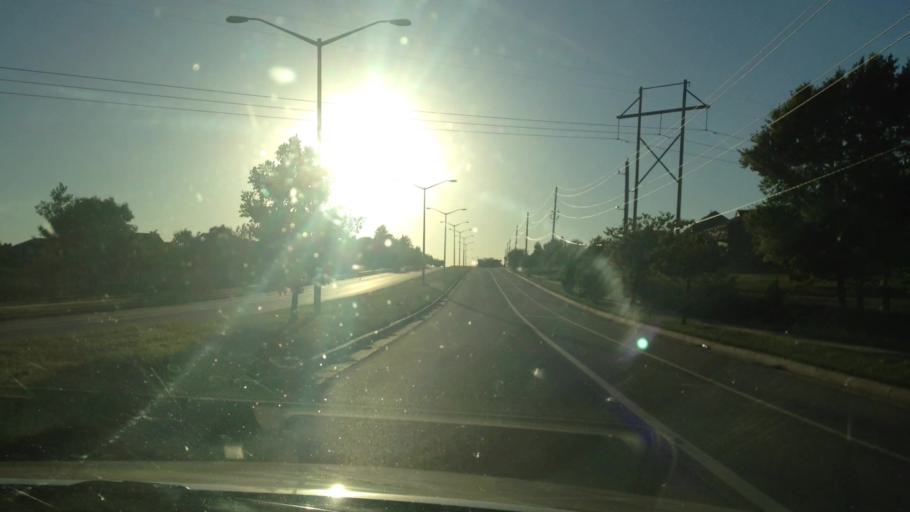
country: US
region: Missouri
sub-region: Clay County
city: Pleasant Valley
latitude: 39.2885
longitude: -94.4817
